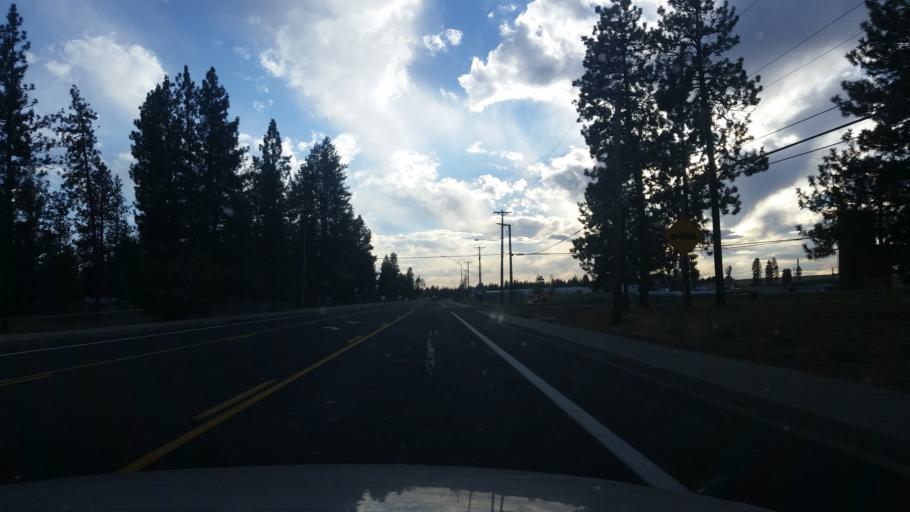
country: US
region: Washington
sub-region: Spokane County
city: Cheney
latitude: 47.4768
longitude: -117.5957
